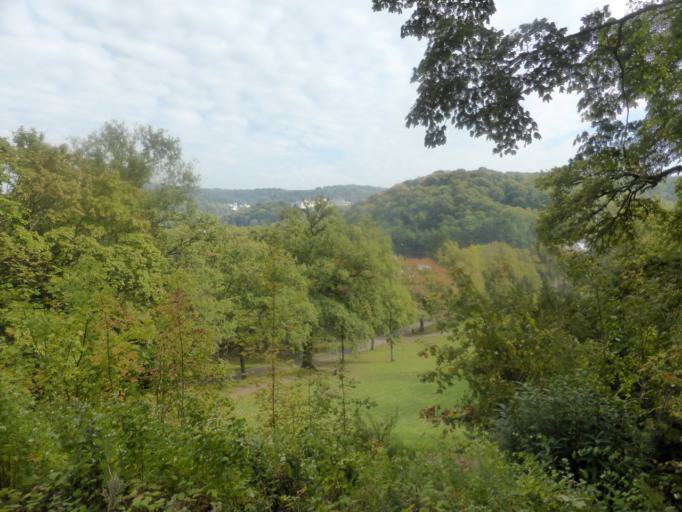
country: FR
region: Lorraine
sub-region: Departement de la Moselle
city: Forbach
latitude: 49.1832
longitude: 6.9013
